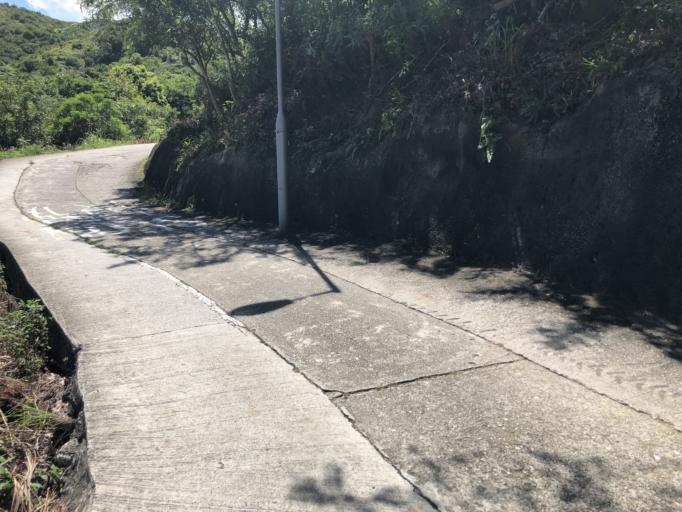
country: HK
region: Tuen Mun
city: Tuen Mun
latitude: 22.2934
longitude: 113.9754
